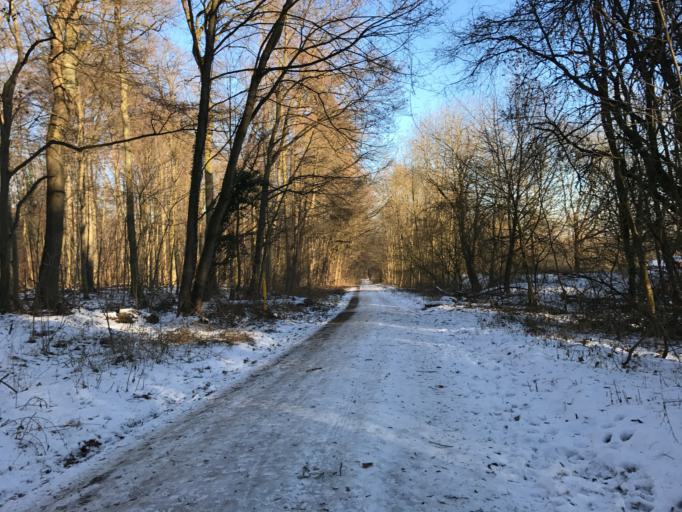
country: DE
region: Hesse
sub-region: Regierungsbezirk Darmstadt
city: Hofheim am Taunus
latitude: 50.0795
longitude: 8.4138
